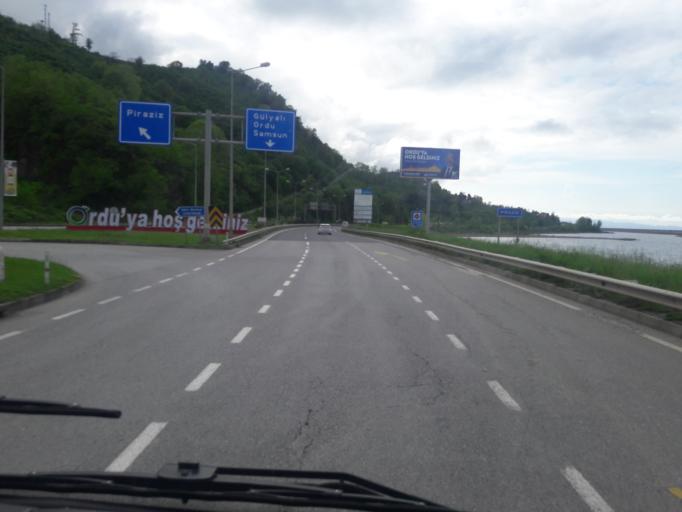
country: TR
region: Giresun
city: Piraziz
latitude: 40.9580
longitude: 38.1142
